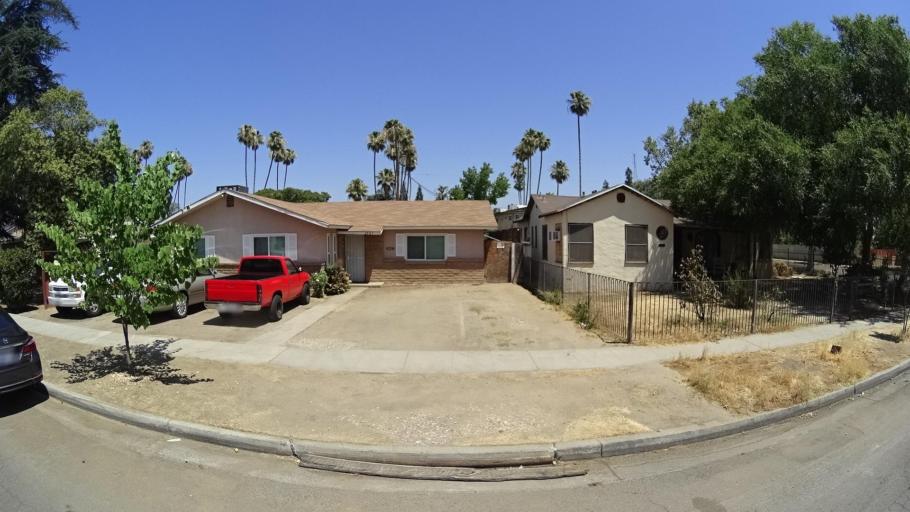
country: US
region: California
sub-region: Fresno County
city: Fresno
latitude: 36.7686
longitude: -119.7751
